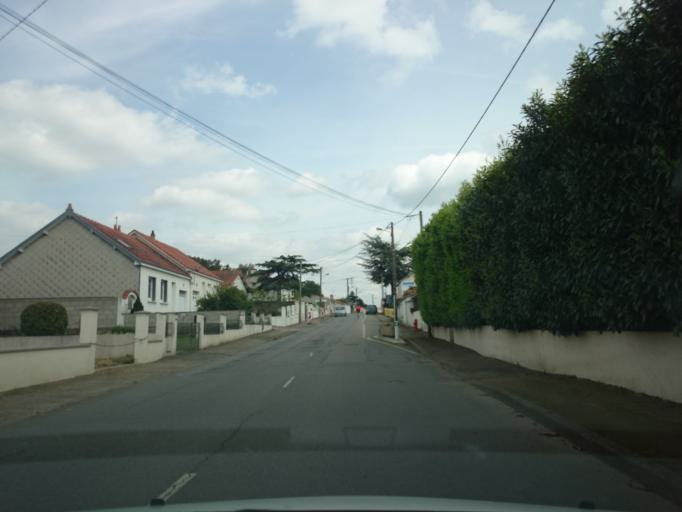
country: FR
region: Pays de la Loire
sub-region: Departement de la Loire-Atlantique
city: Pont-Saint-Martin
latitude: 47.1242
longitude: -1.5906
